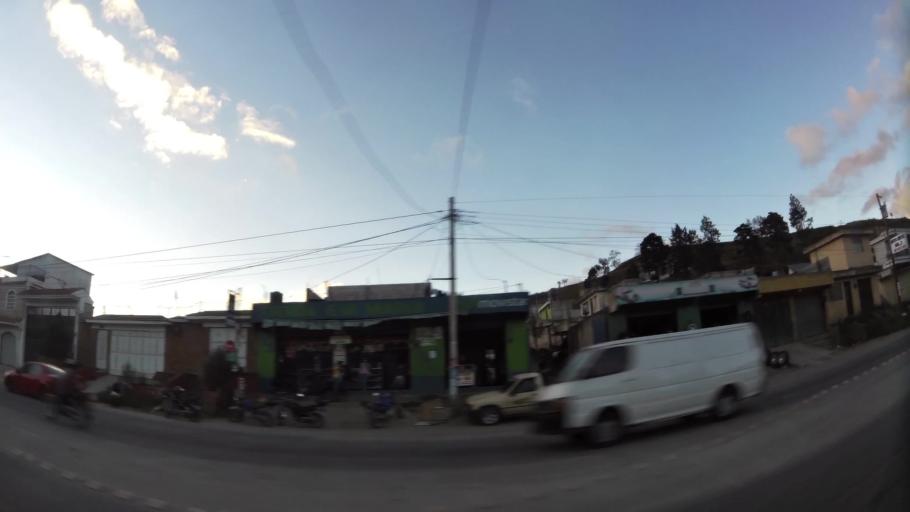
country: GT
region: Quetzaltenango
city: Salcaja
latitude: 14.8587
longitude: -91.4731
